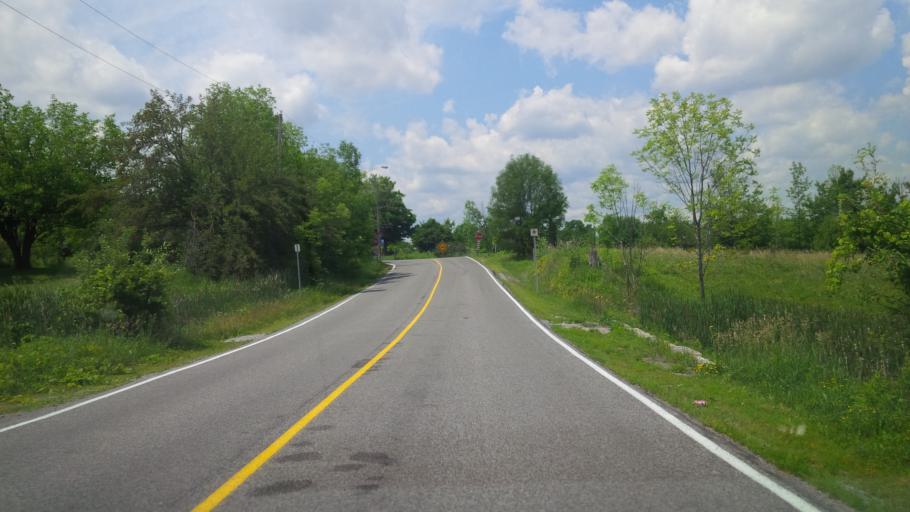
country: CA
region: Ontario
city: Burlington
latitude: 43.4185
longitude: -79.8592
